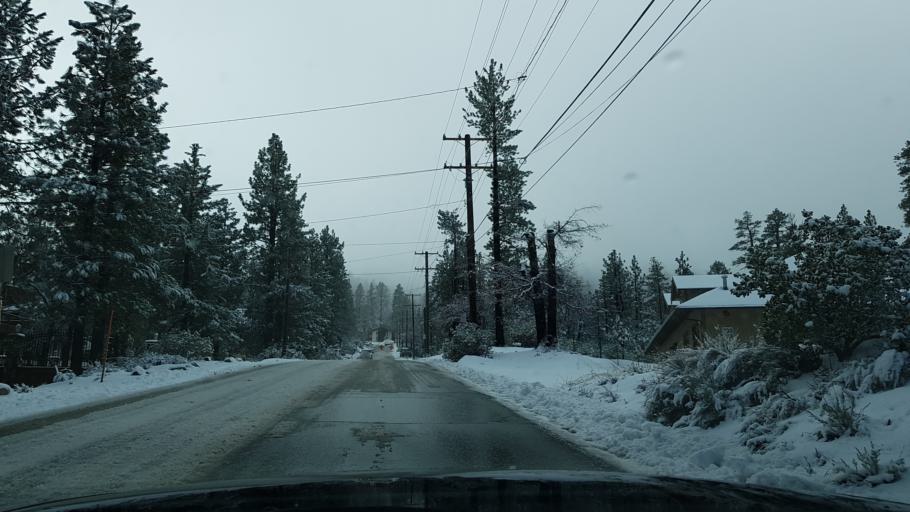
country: US
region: California
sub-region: San Bernardino County
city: Big Bear Lake
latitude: 34.2398
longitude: -116.8924
